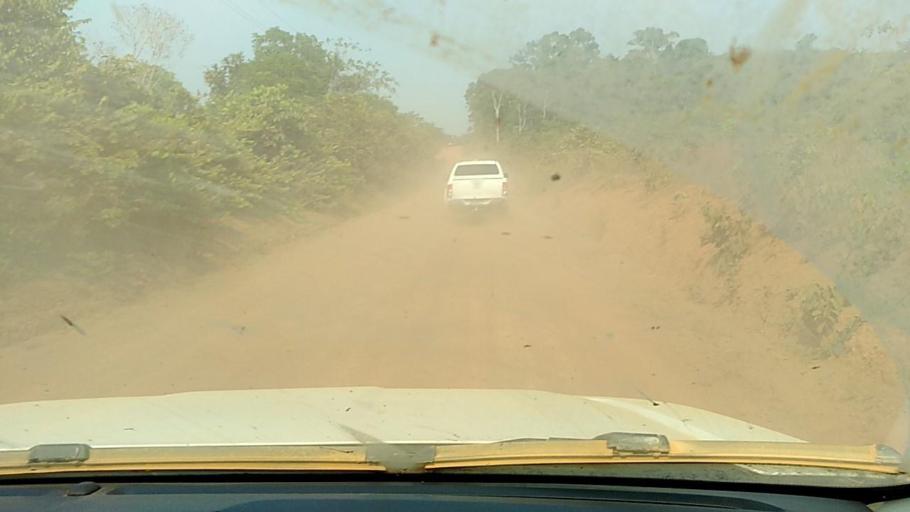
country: BR
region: Rondonia
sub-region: Porto Velho
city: Porto Velho
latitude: -8.8433
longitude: -64.1588
